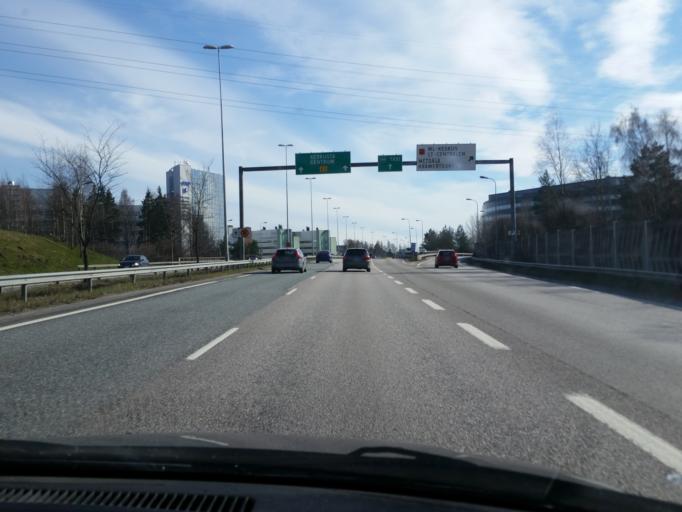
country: FI
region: Uusimaa
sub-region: Helsinki
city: Helsinki
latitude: 60.2230
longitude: 24.9451
